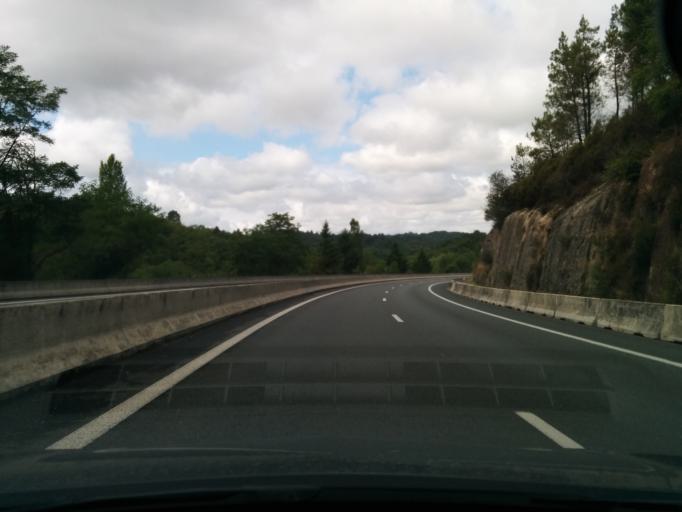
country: FR
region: Limousin
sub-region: Departement de la Correze
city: Brive-la-Gaillarde
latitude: 45.1075
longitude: 1.5098
